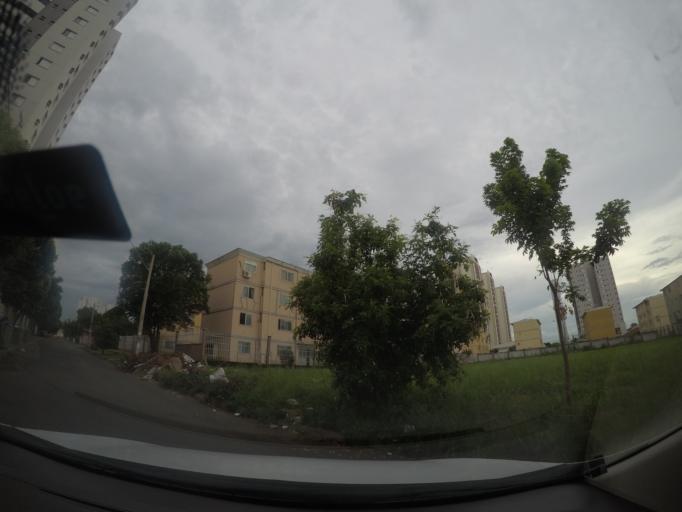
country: BR
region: Goias
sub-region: Goiania
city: Goiania
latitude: -16.6494
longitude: -49.2464
